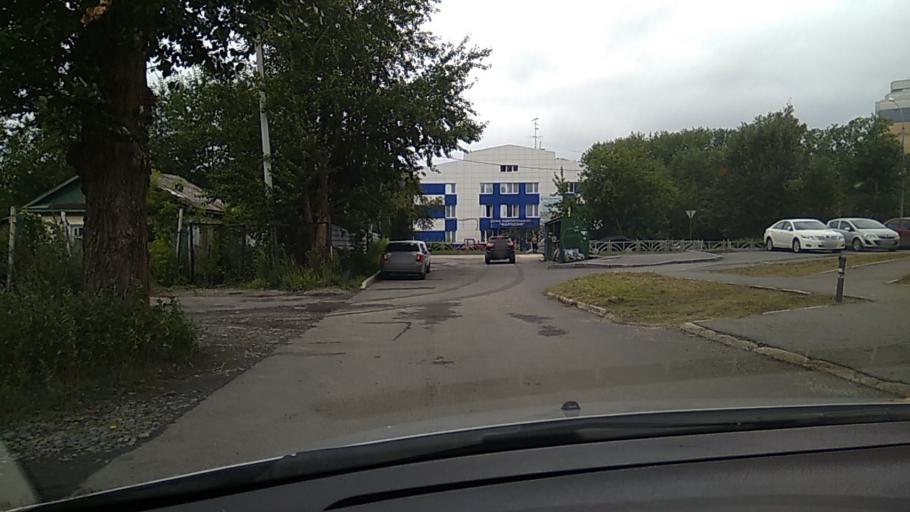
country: RU
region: Sverdlovsk
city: Sovkhoznyy
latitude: 56.7677
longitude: 60.6048
